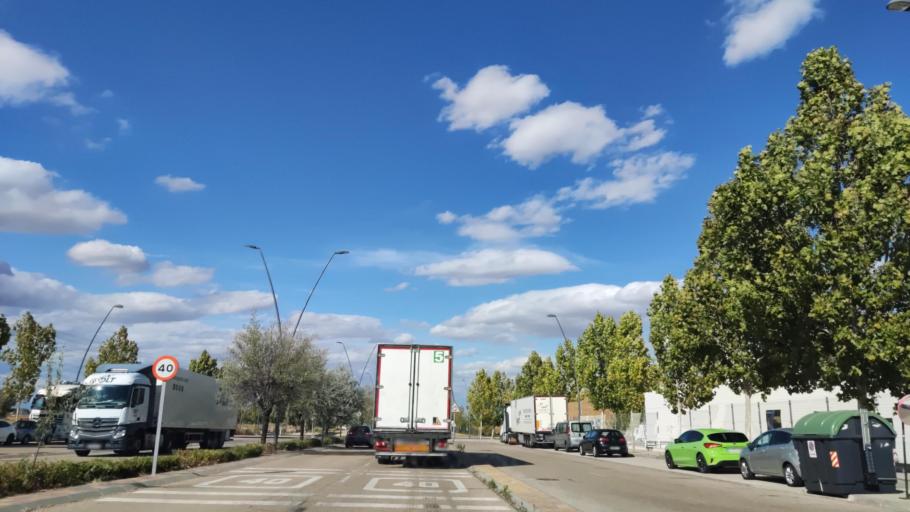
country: ES
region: Madrid
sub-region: Provincia de Madrid
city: Pinto
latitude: 40.2817
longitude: -3.6805
